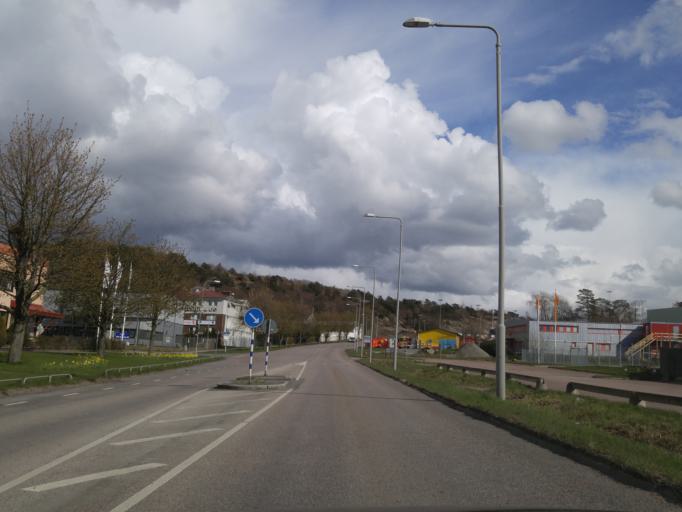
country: SE
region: Vaestra Goetaland
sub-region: Goteborg
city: Majorna
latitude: 57.6587
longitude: 11.9437
